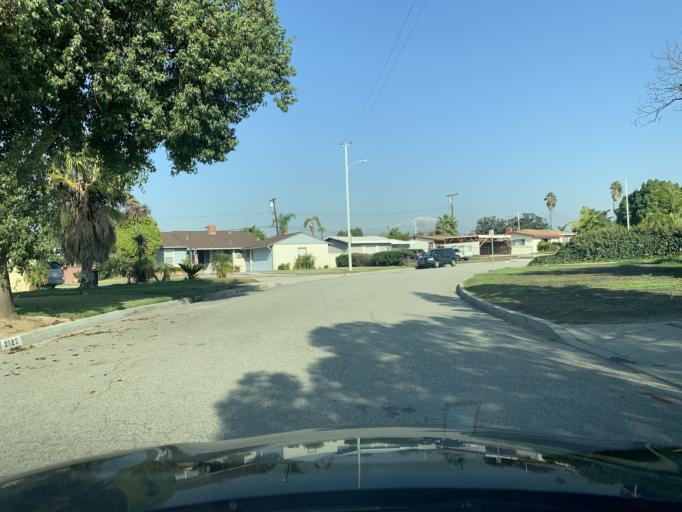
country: US
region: California
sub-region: Los Angeles County
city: Covina
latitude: 34.0736
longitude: -117.9001
